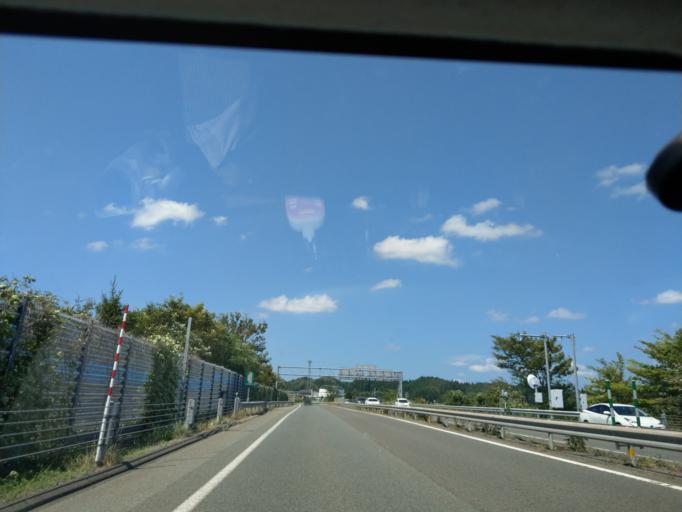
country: JP
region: Akita
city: Akita
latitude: 39.6480
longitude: 140.2073
